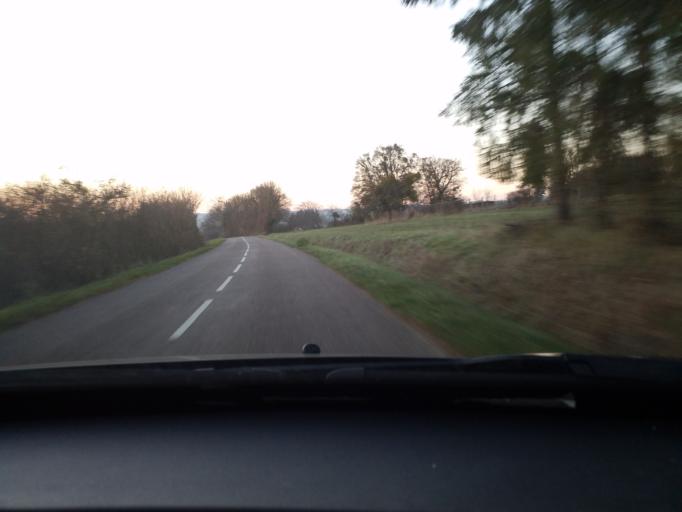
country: FR
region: Franche-Comte
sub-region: Departement de la Haute-Saone
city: Faverney
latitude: 47.8846
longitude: 6.1373
